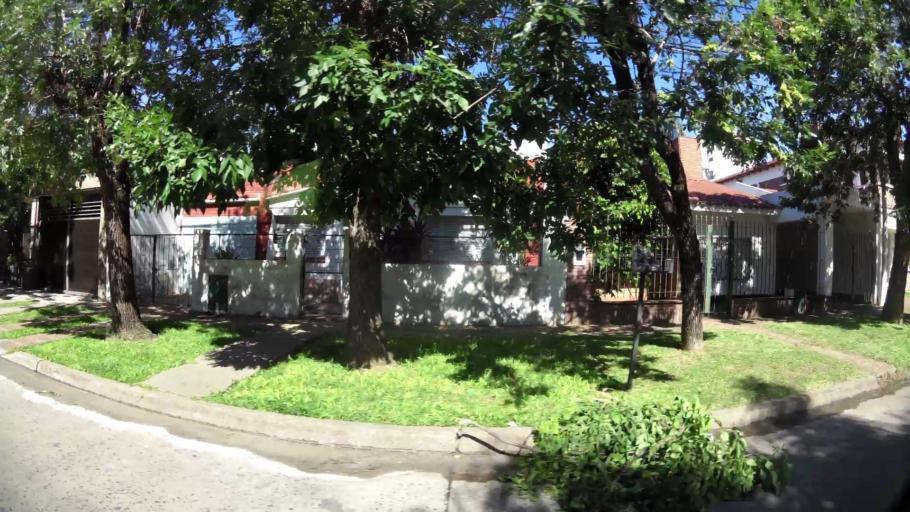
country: AR
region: Santa Fe
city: Santa Fe de la Vera Cruz
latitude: -31.6189
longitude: -60.6786
